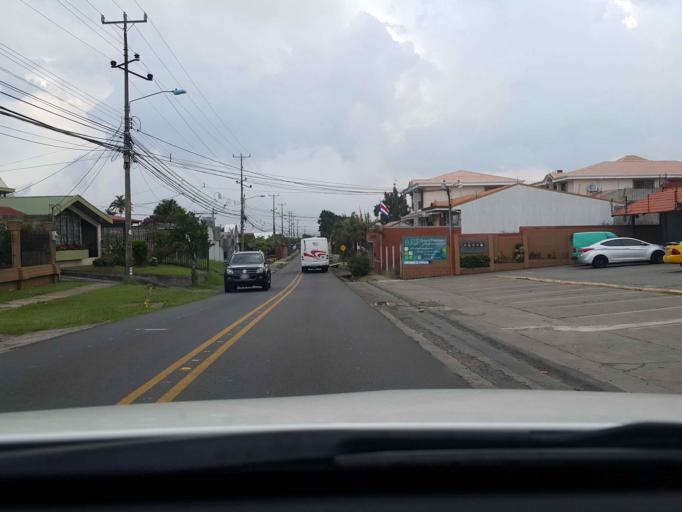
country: CR
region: Heredia
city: San Pablo
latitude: 10.0007
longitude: -84.0973
